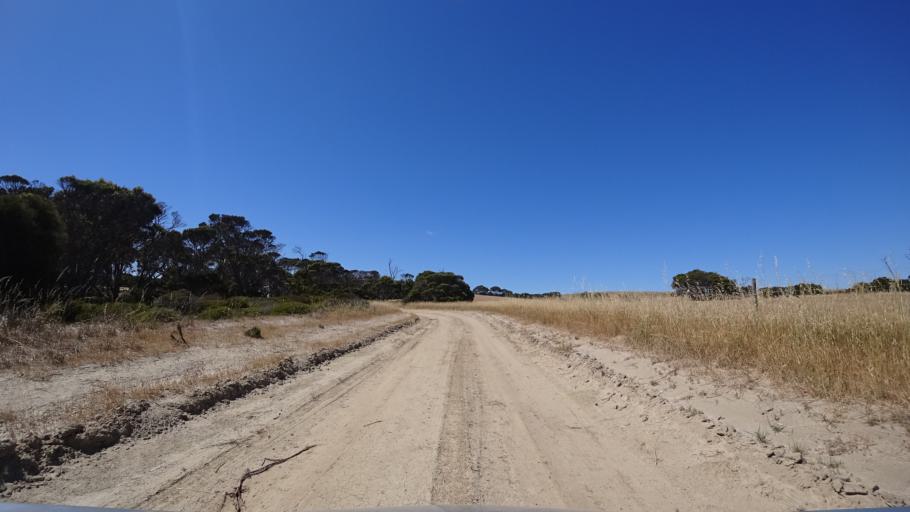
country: AU
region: South Australia
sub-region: Kangaroo Island
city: Kingscote
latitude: -35.7374
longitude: 137.7185
